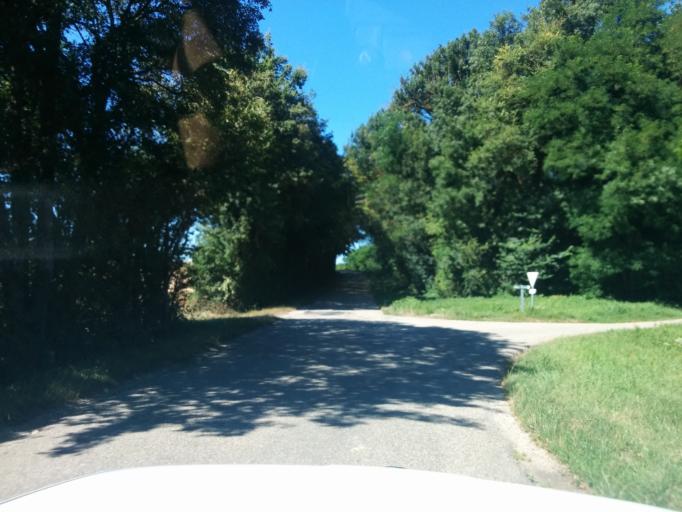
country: FR
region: Rhone-Alpes
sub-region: Departement de l'Ain
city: Perouges
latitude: 45.9187
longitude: 5.1498
